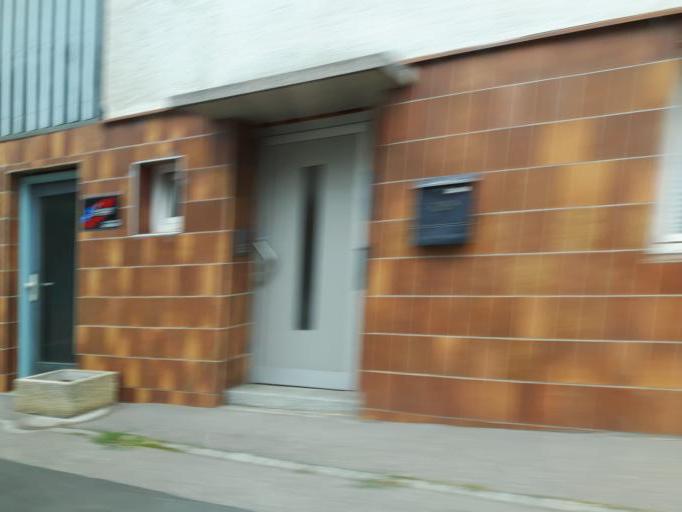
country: DE
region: Baden-Wuerttemberg
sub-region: Regierungsbezirk Stuttgart
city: Eberstadt
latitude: 49.1796
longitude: 9.3448
